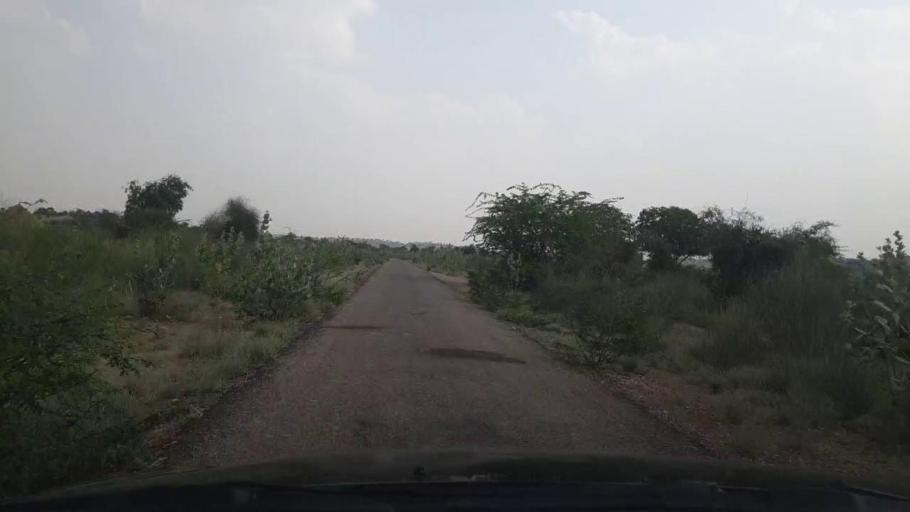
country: PK
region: Sindh
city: Islamkot
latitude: 25.0083
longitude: 70.5969
